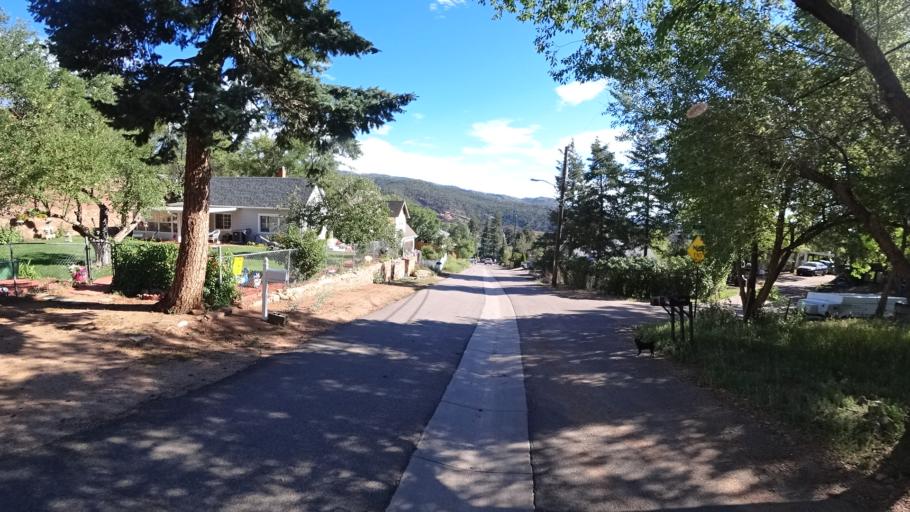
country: US
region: Colorado
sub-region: El Paso County
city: Manitou Springs
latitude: 38.8525
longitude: -104.9153
